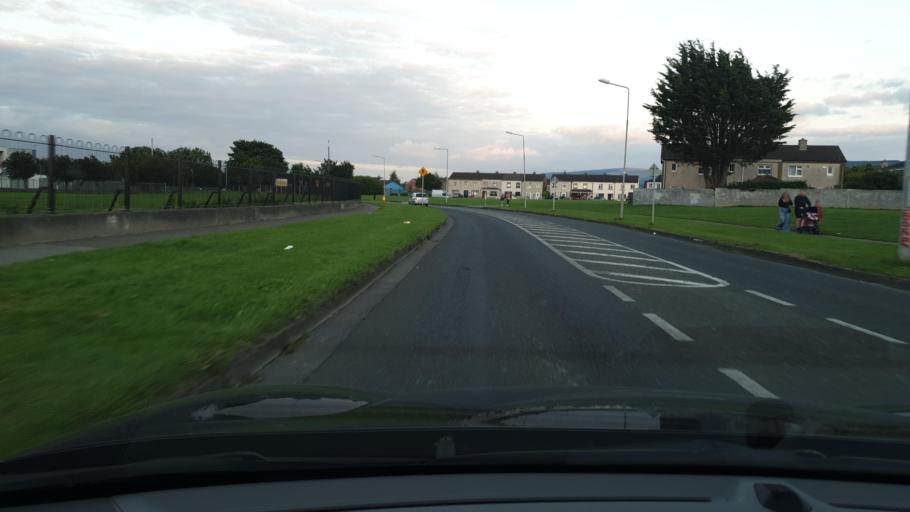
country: IE
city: Jobstown
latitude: 53.2826
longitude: -6.3957
